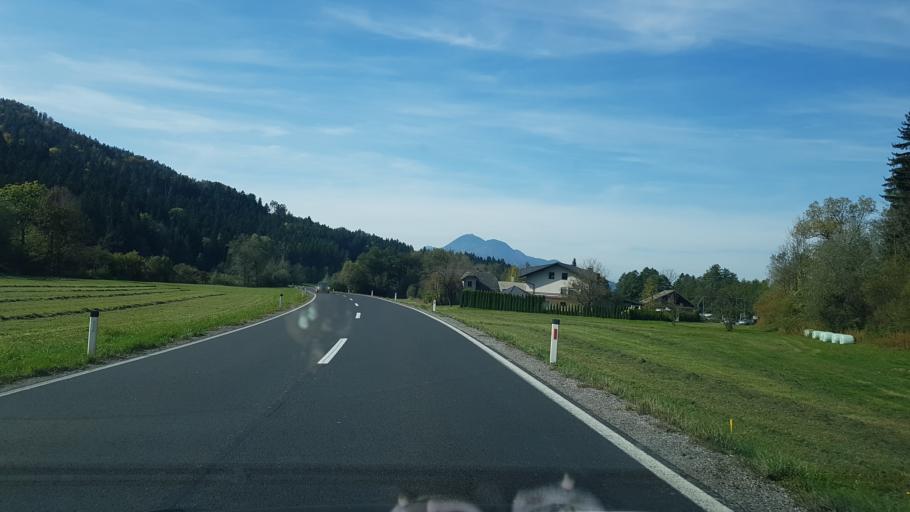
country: SI
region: Slovenj Gradec
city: Legen
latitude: 46.4489
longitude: 15.1671
